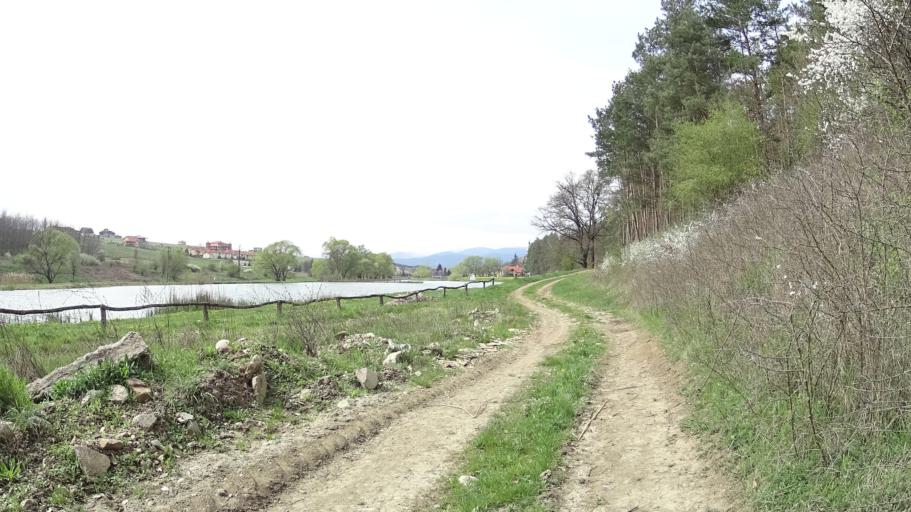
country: HU
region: Nograd
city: Diosjeno
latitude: 47.8835
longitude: 19.0779
